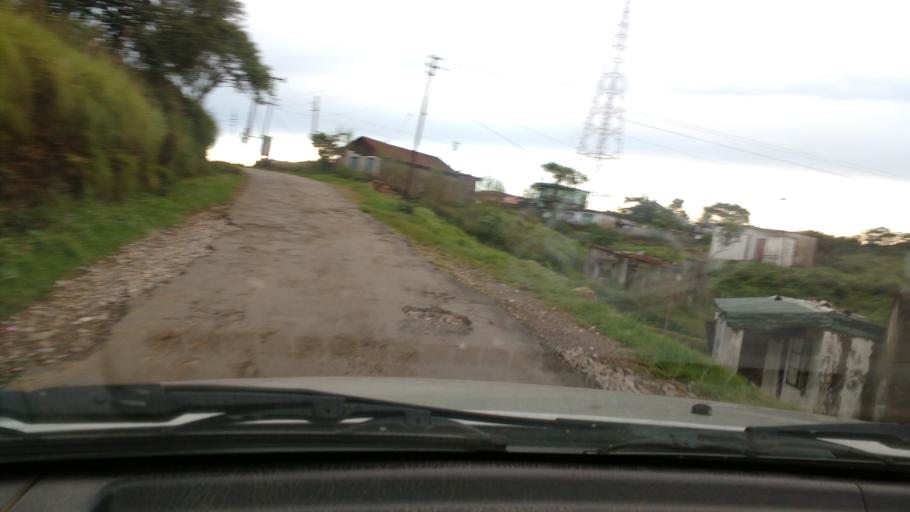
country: IN
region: Meghalaya
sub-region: East Khasi Hills
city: Cherrapunji
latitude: 25.2844
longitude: 91.7158
